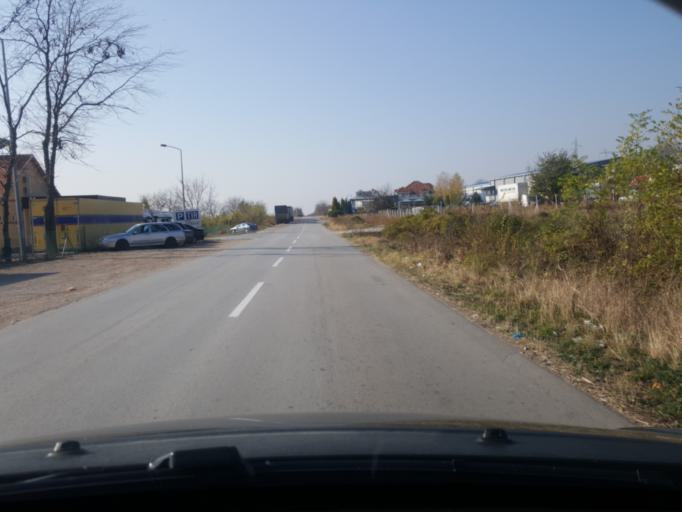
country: RS
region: Central Serbia
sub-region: Nisavski Okrug
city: Niska Banja
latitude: 43.3191
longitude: 22.0163
